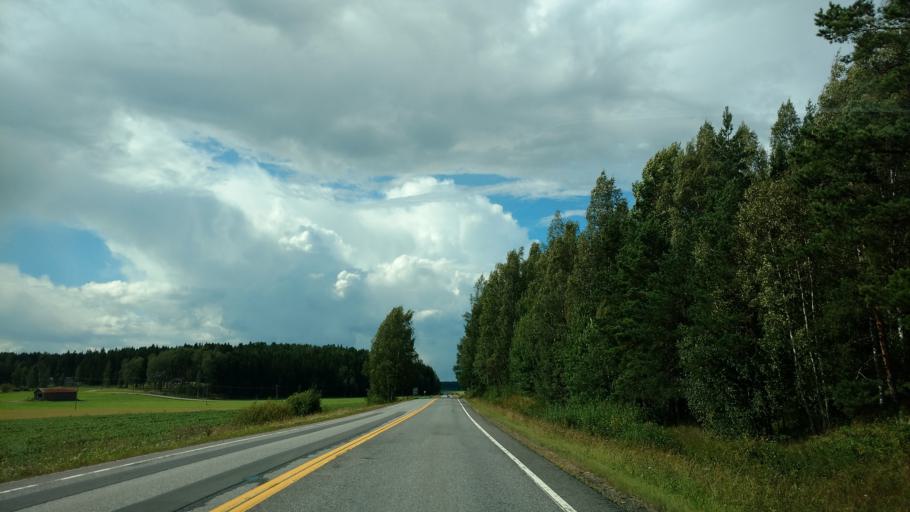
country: FI
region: Varsinais-Suomi
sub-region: Salo
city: Halikko
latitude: 60.3837
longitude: 22.8903
